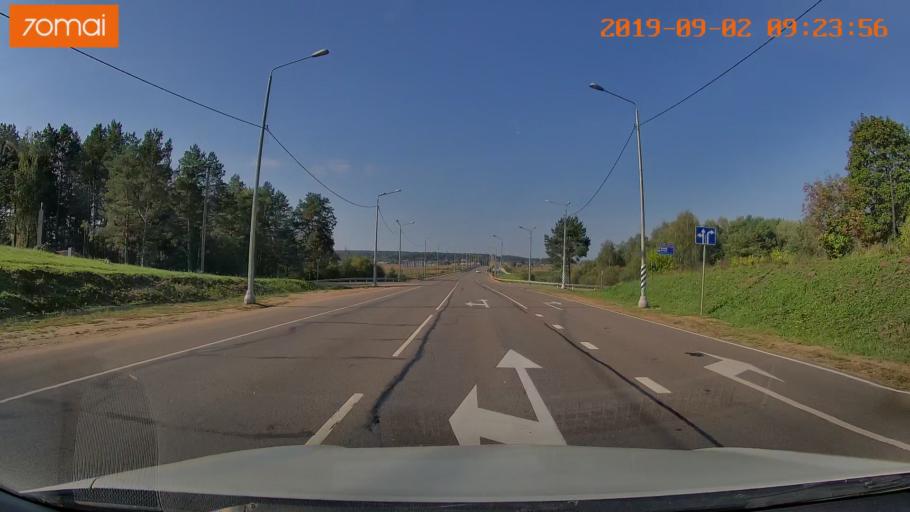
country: RU
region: Kaluga
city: Yukhnov
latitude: 54.7709
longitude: 35.3043
